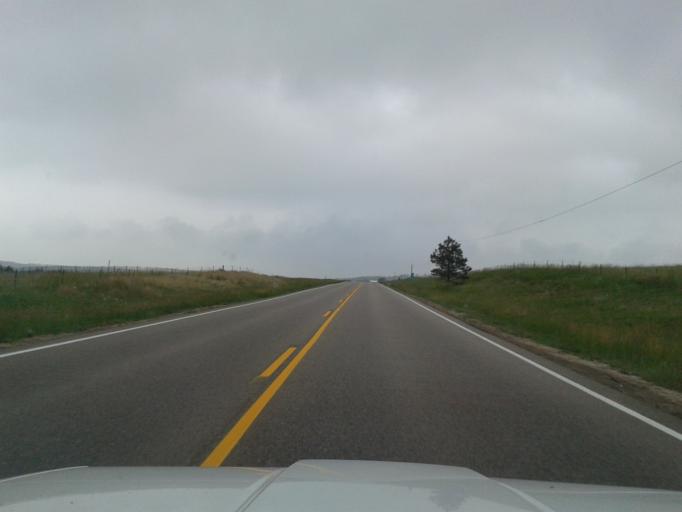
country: US
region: Colorado
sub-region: El Paso County
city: Woodmoor
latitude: 39.1641
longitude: -104.7466
